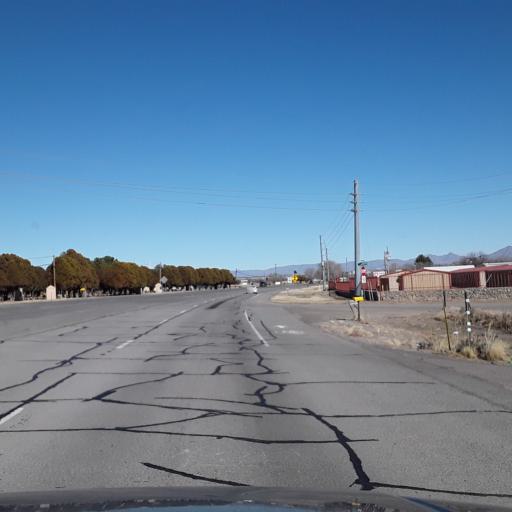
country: US
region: New Mexico
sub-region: Dona Ana County
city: Mesilla
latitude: 32.2996
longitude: -106.8541
